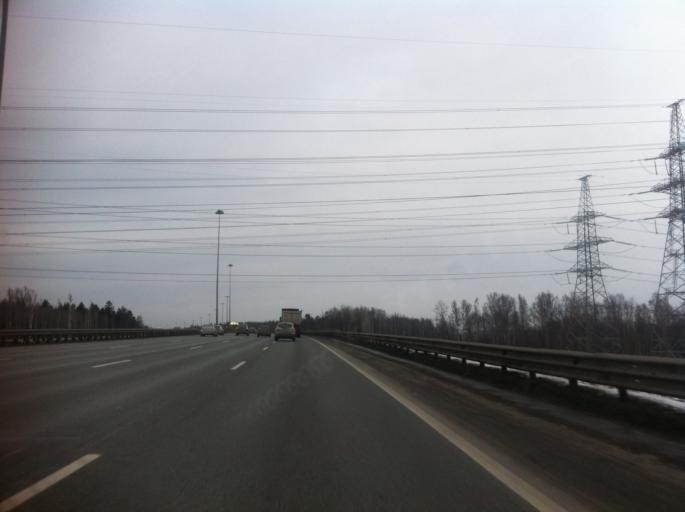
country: RU
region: Leningrad
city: Rybatskoye
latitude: 59.9084
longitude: 30.5264
